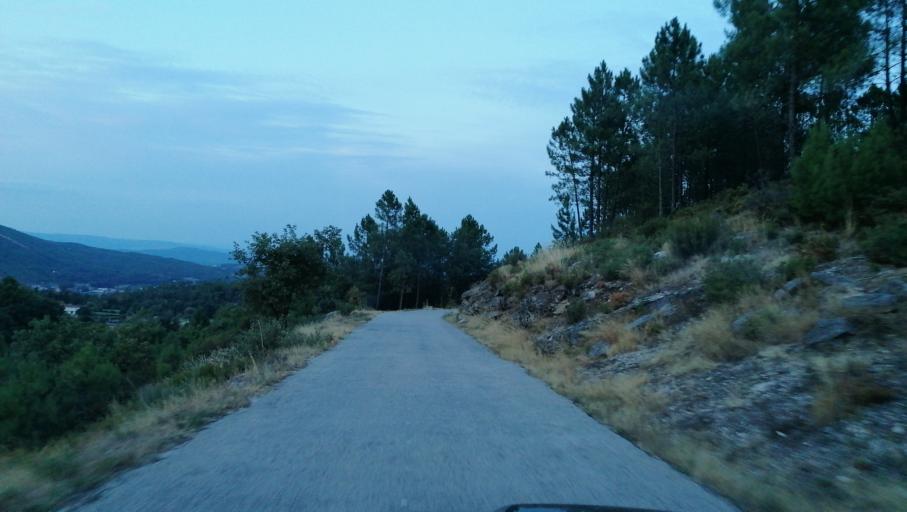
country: PT
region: Vila Real
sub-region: Vila Pouca de Aguiar
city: Vila Pouca de Aguiar
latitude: 41.5558
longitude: -7.6539
